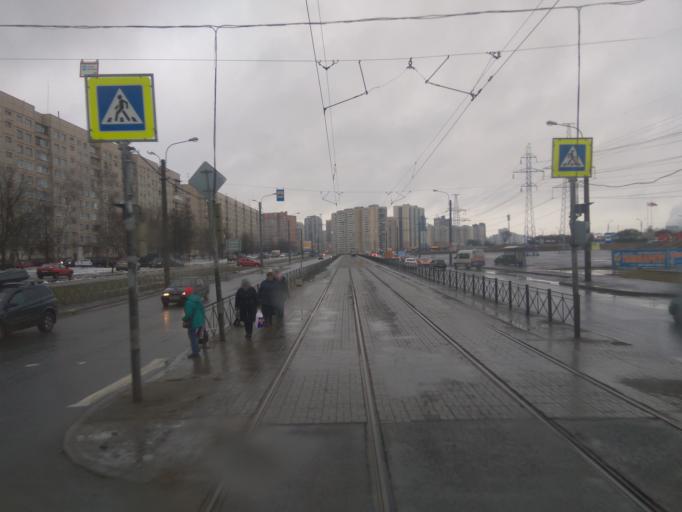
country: RU
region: St.-Petersburg
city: Uritsk
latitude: 59.8600
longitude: 30.2135
